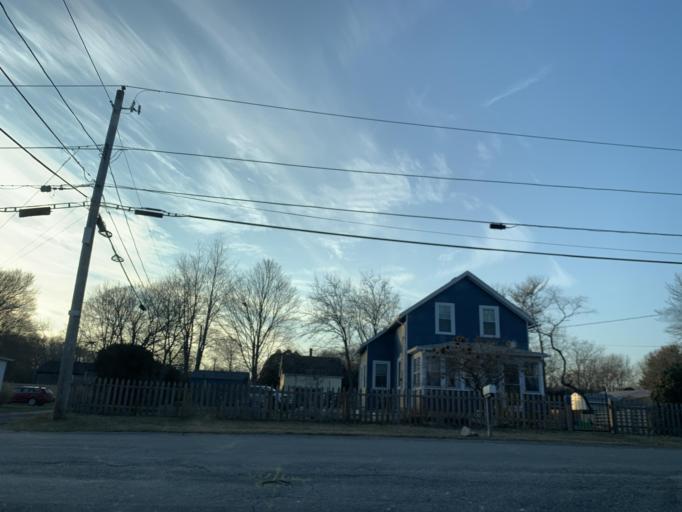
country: US
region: Rhode Island
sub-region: Washington County
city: Wakefield-Peacedale
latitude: 41.4494
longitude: -71.5067
